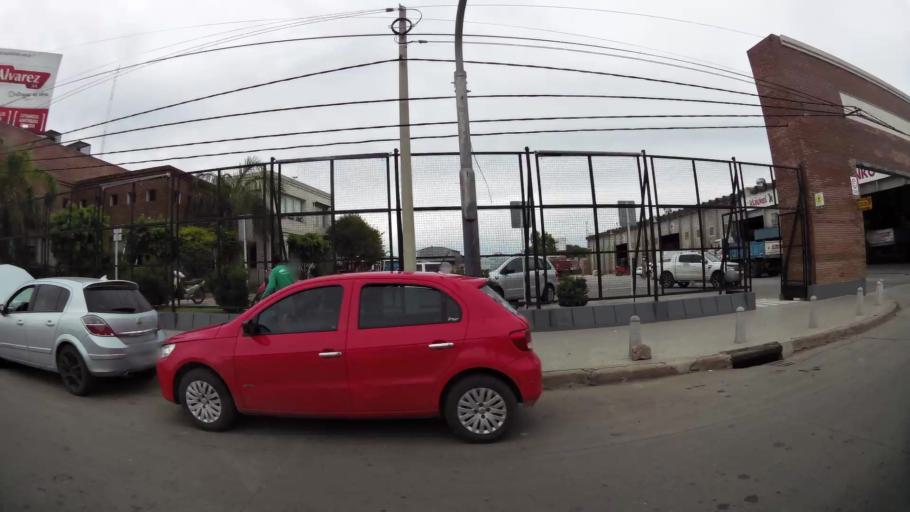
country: AR
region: Santa Fe
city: Gobernador Galvez
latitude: -32.9912
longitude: -60.6641
